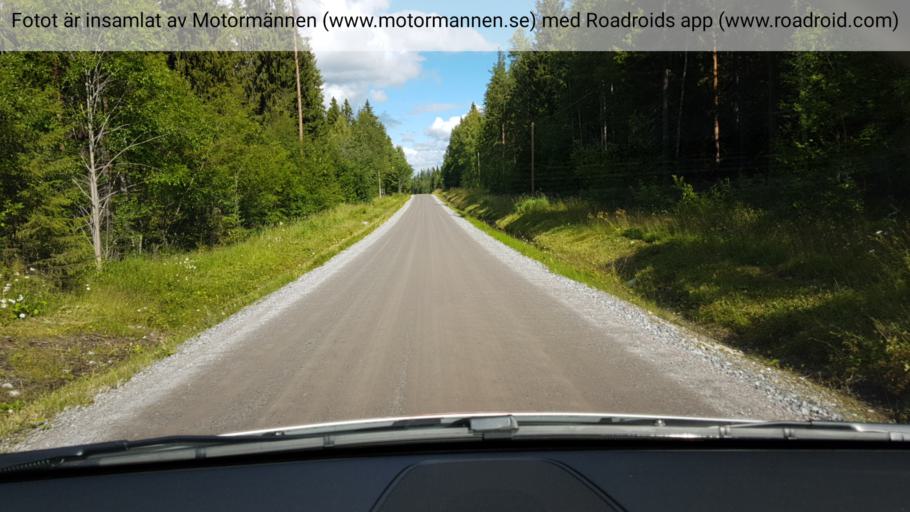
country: SE
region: Jaemtland
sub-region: Braecke Kommun
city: Braecke
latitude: 63.1257
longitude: 15.7558
